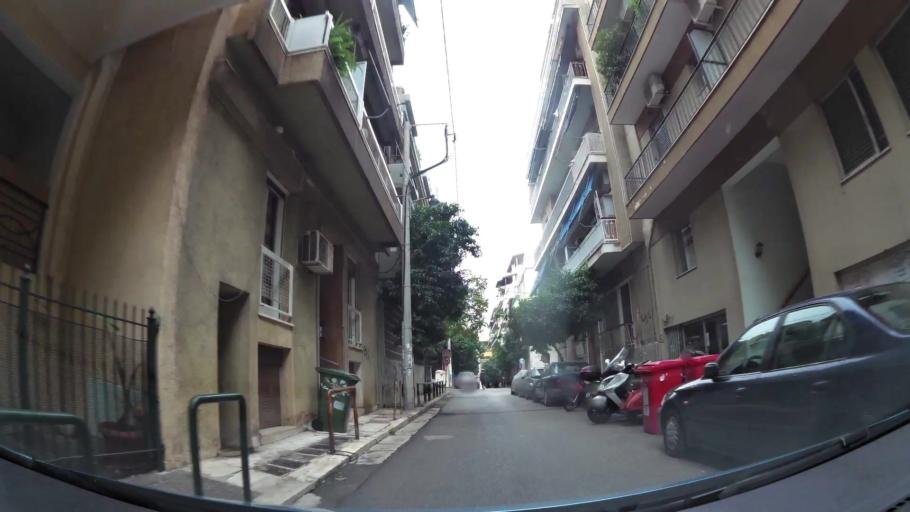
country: GR
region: Attica
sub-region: Nomarchia Athinas
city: Vyronas
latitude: 37.9631
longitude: 23.7548
